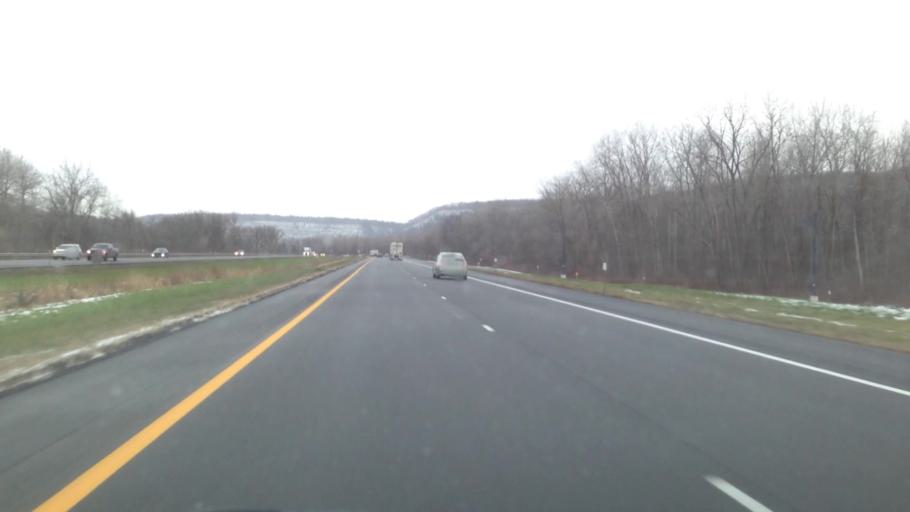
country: US
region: New York
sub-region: Montgomery County
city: Fonda
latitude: 42.9144
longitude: -74.4462
